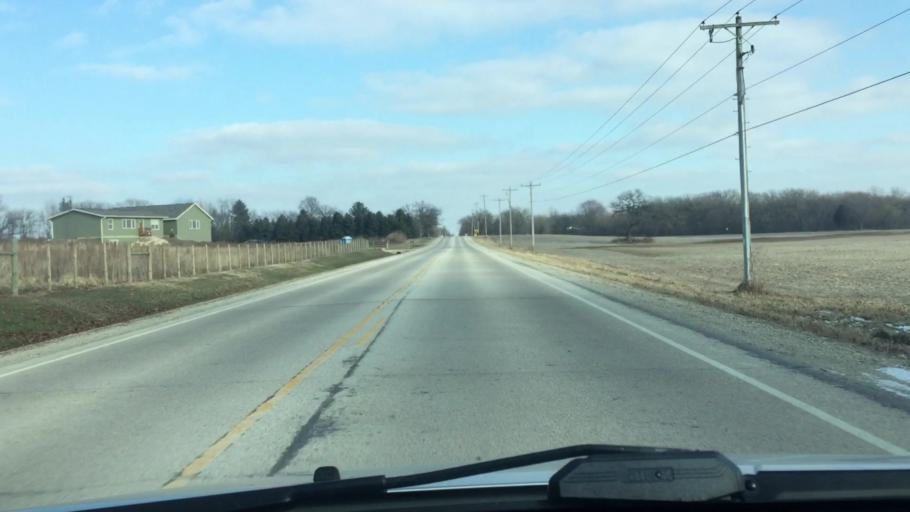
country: US
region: Wisconsin
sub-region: Jefferson County
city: Palmyra
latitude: 42.9022
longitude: -88.5471
